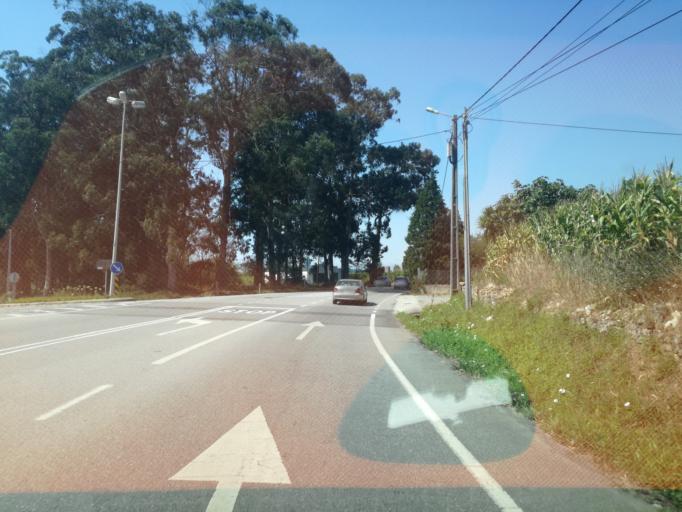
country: PT
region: Braga
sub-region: Esposende
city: Apulia
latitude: 41.4812
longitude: -8.7485
